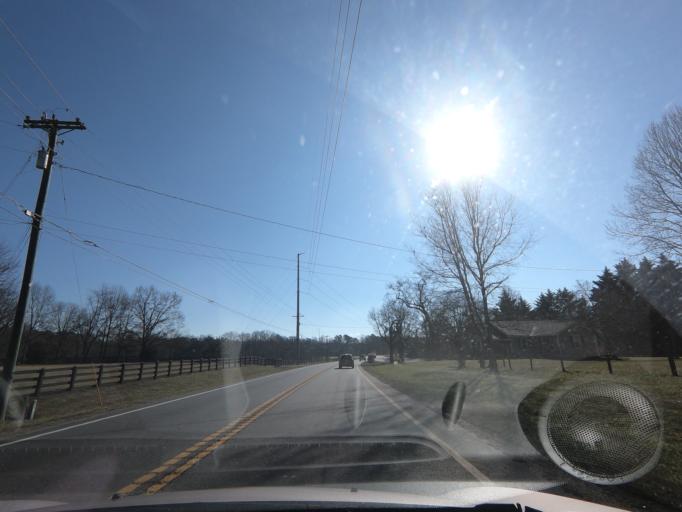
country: US
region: Georgia
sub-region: Forsyth County
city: Cumming
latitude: 34.2994
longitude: -84.1655
